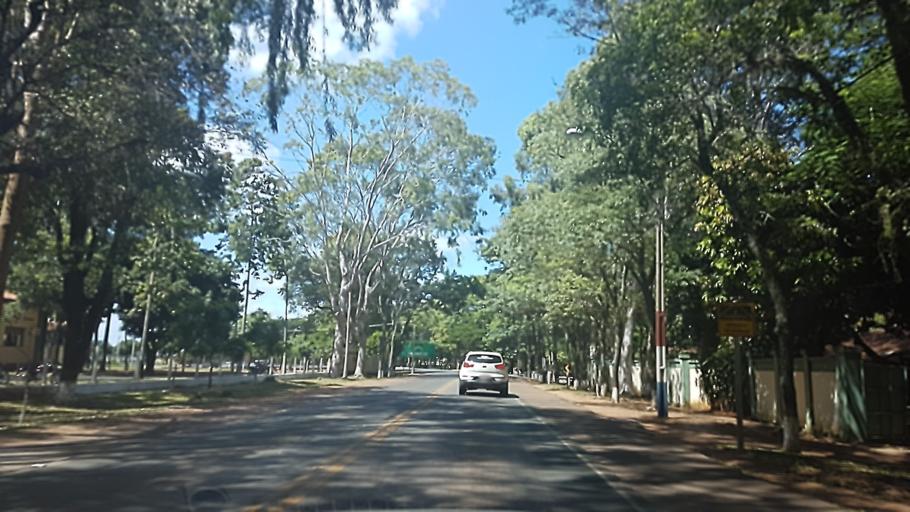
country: PY
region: Misiones
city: San Juan Bautista
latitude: -26.6691
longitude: -57.1344
